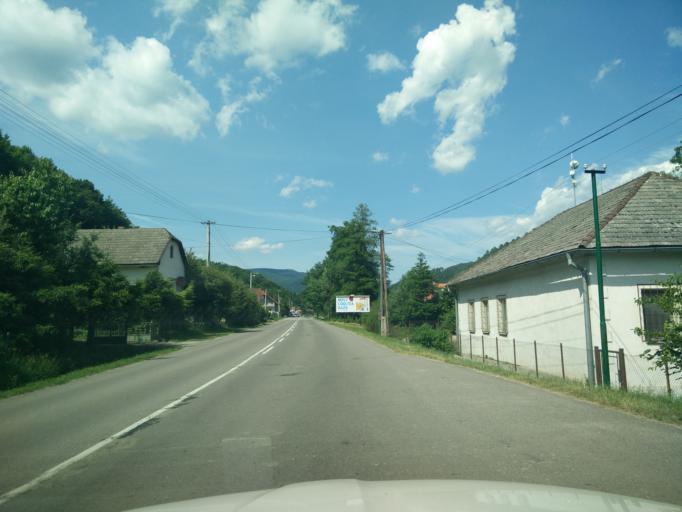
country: SK
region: Nitriansky
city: Prievidza
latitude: 48.9003
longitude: 18.6490
